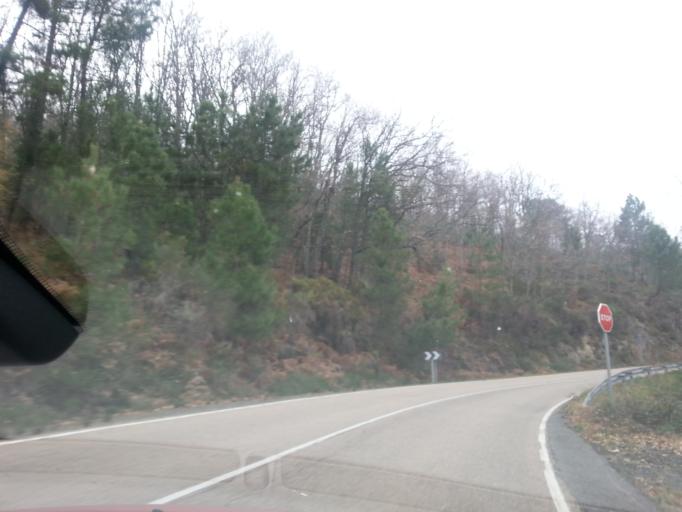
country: ES
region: Castille and Leon
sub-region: Provincia de Salamanca
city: Madronal
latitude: 40.4654
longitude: -6.0664
